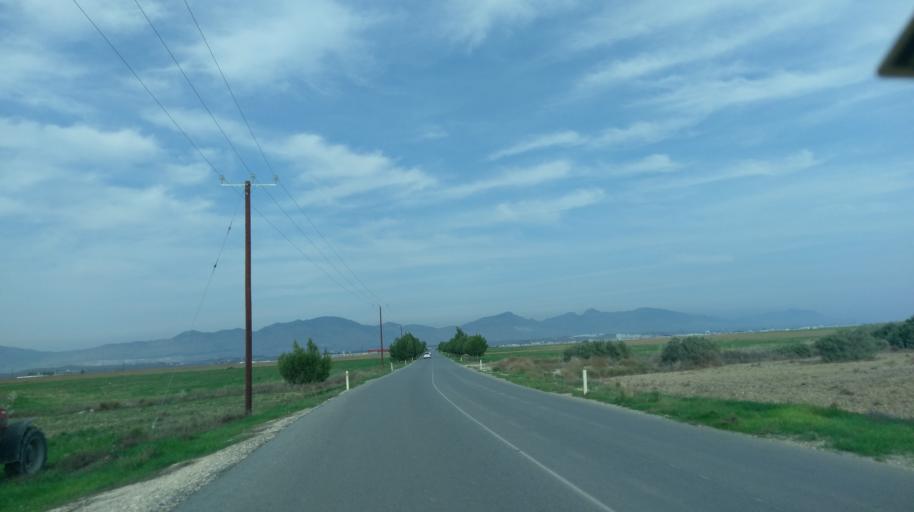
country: CY
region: Lefkosia
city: Mammari
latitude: 35.1985
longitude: 33.2673
